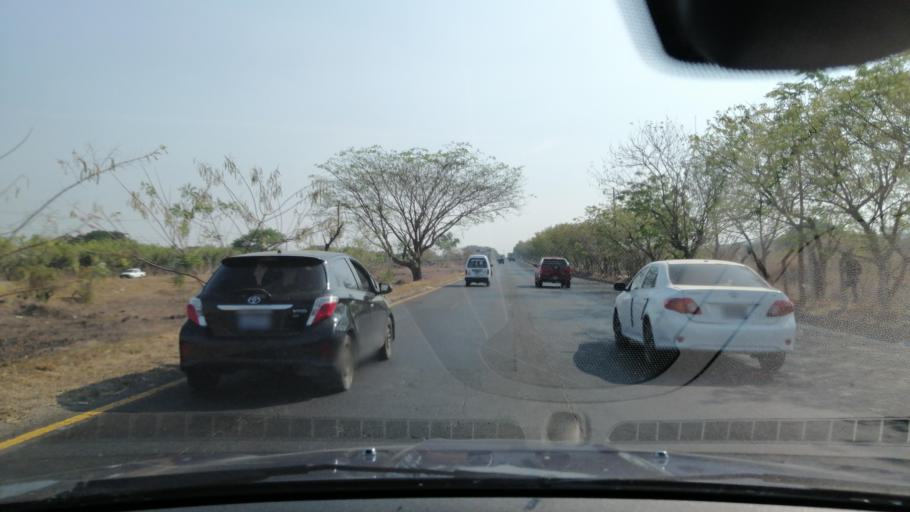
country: SV
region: La Libertad
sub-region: Distrito de Quezaltepeque
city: Quezaltepeque
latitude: 13.8030
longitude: -89.3319
